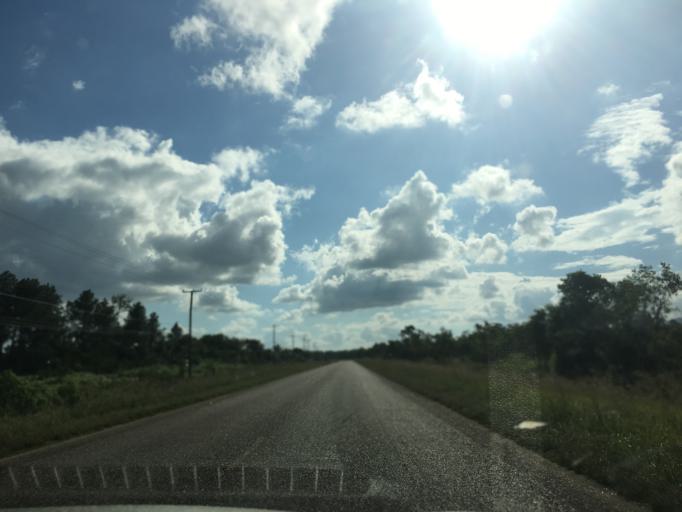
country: BZ
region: Stann Creek
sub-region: Dangriga
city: Dangriga
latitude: 16.8790
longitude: -88.3435
